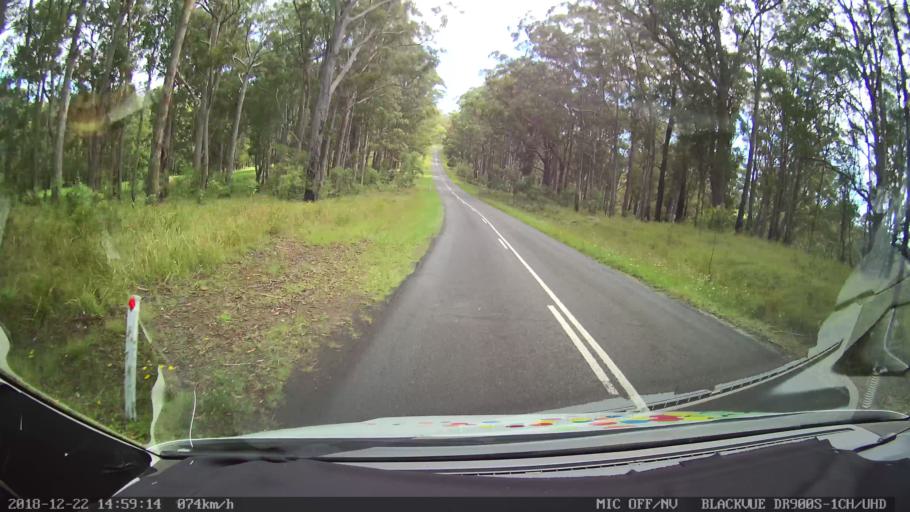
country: AU
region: New South Wales
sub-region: Bellingen
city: Dorrigo
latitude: -30.2450
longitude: 152.4831
